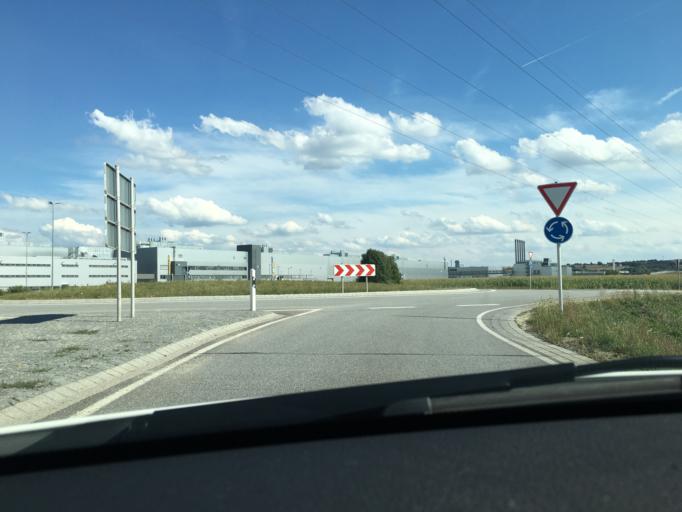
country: DE
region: Bavaria
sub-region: Lower Bavaria
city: Loiching
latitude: 48.6475
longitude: 12.4545
